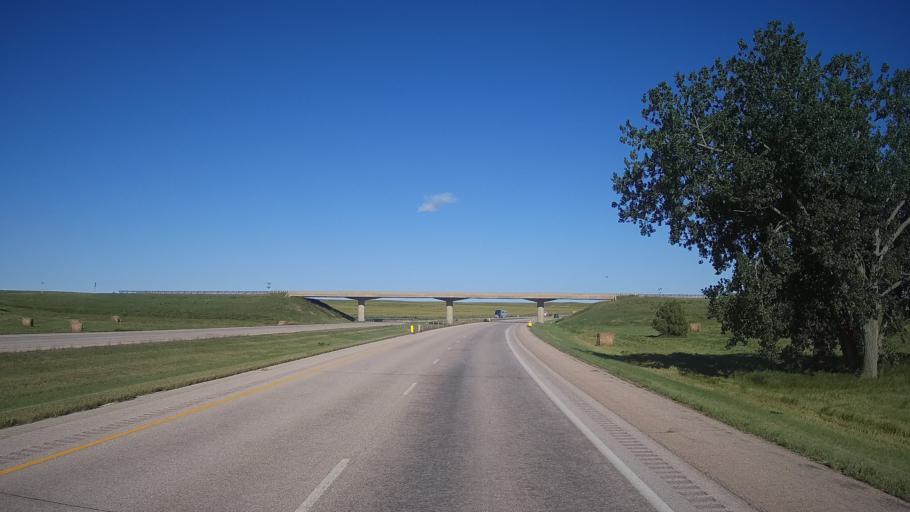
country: US
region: South Dakota
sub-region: Pennington County
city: Box Elder
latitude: 44.1061
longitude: -102.6306
